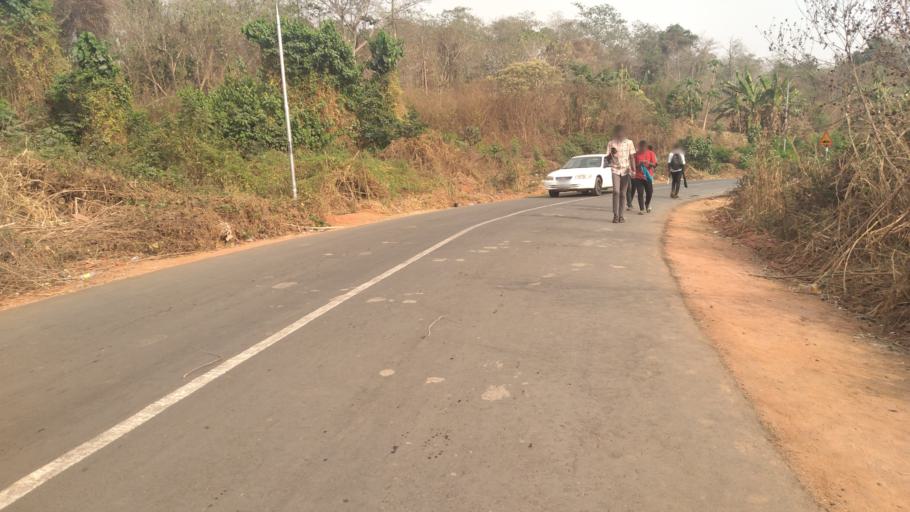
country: NG
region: Ondo
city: Ilare
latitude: 7.3010
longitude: 5.1445
